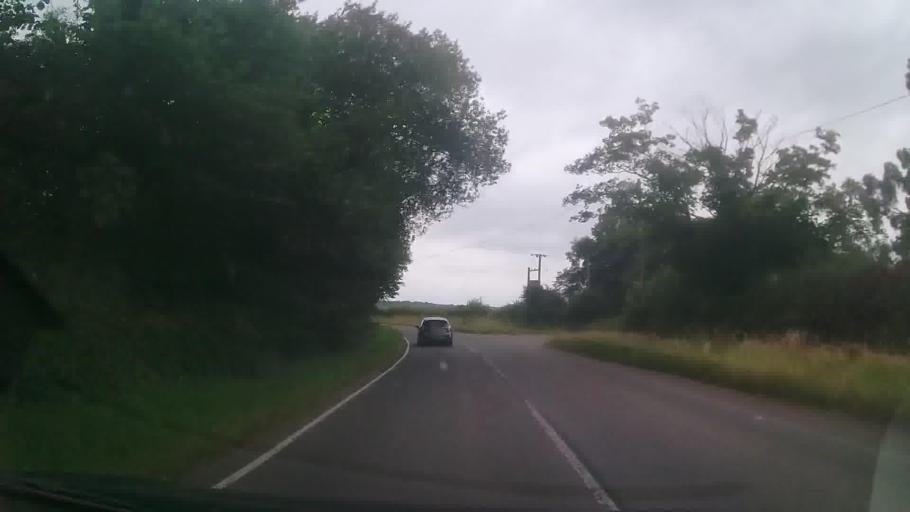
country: GB
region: England
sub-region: Leicestershire
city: Desford
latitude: 52.6526
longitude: -1.2922
